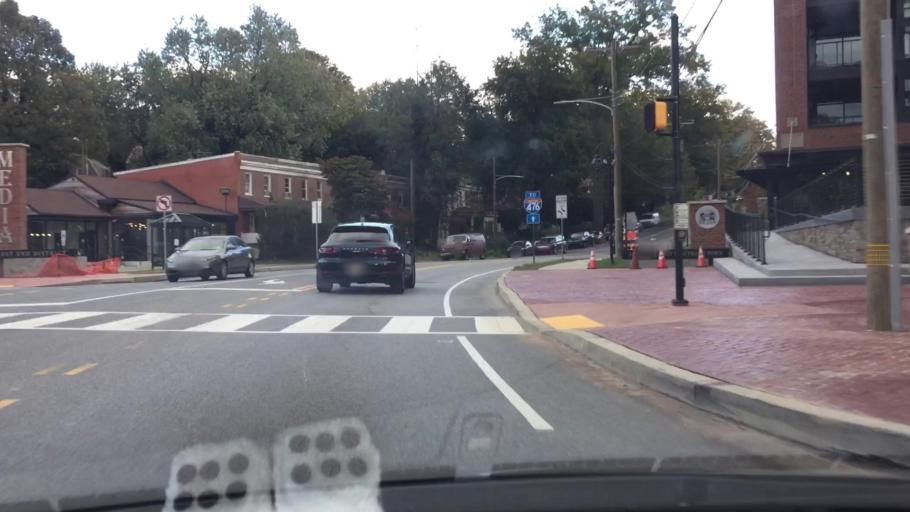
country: US
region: Pennsylvania
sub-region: Delaware County
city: Media
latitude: 39.9178
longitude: -75.3978
